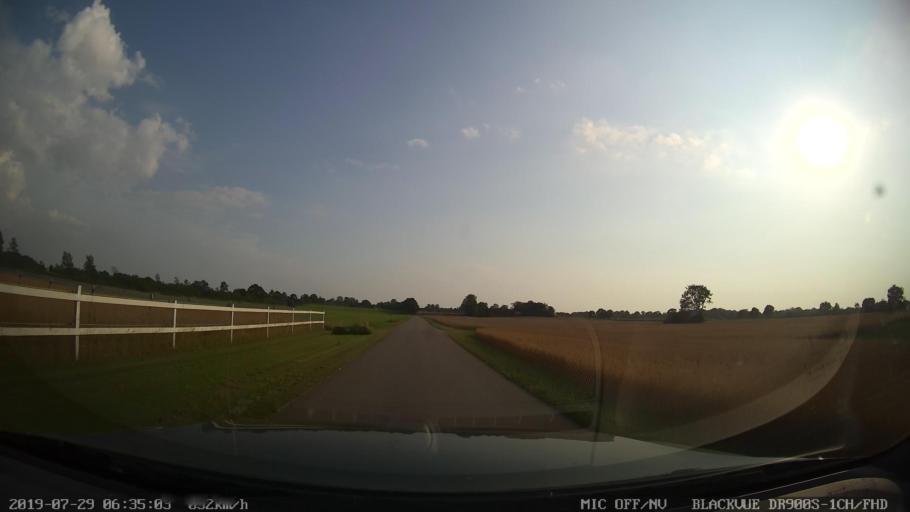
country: SE
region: Skane
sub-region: Helsingborg
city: Odakra
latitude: 56.1160
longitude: 12.7213
